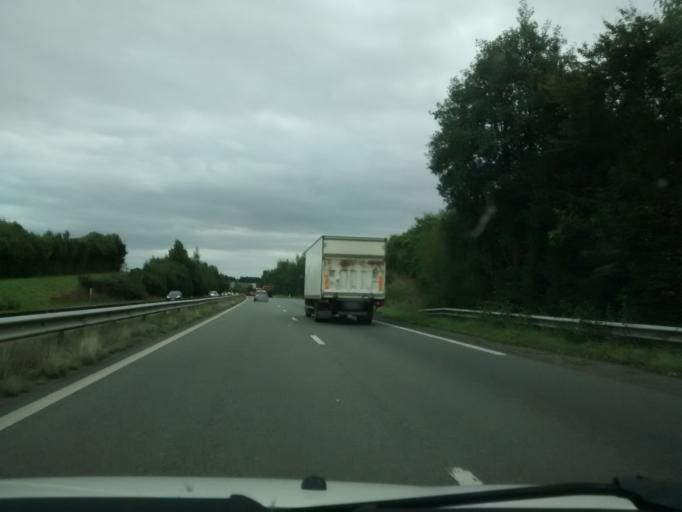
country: FR
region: Brittany
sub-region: Departement d'Ille-et-Vilaine
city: Vignoc
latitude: 48.2580
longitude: -1.7757
